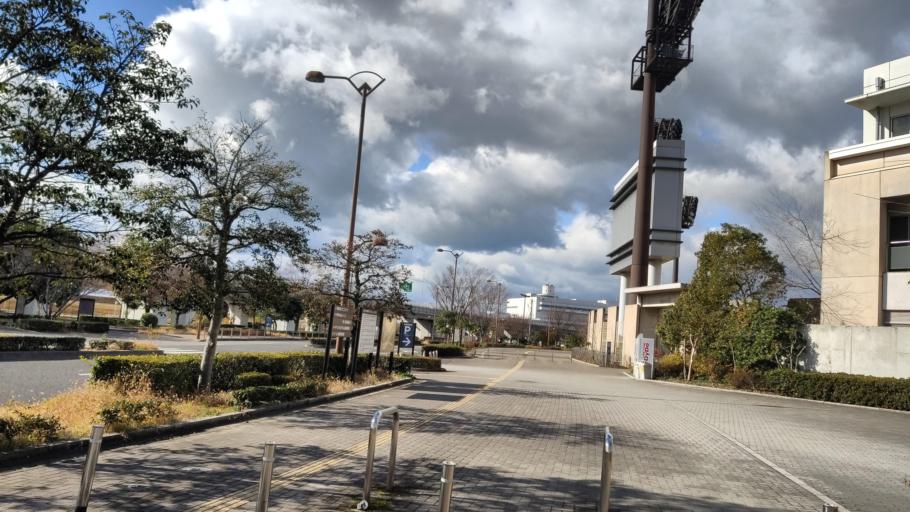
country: JP
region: Ehime
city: Masaki-cho
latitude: 33.8076
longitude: 132.7435
